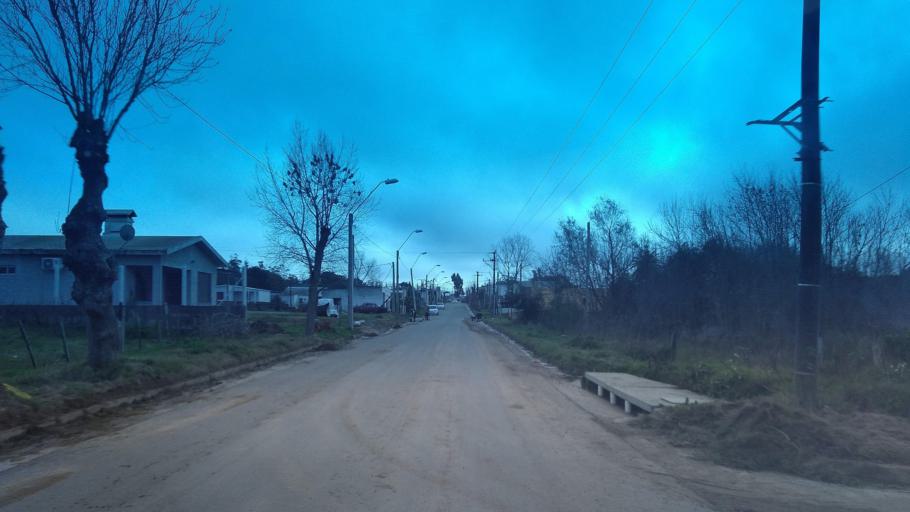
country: UY
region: Canelones
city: Tala
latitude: -34.1991
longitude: -55.7406
